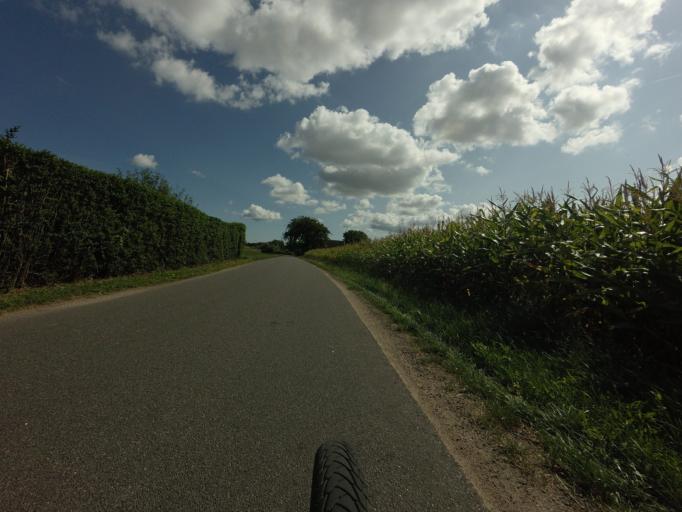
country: DK
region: Zealand
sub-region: Vordingborg Kommune
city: Stege
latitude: 54.9733
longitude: 12.3762
